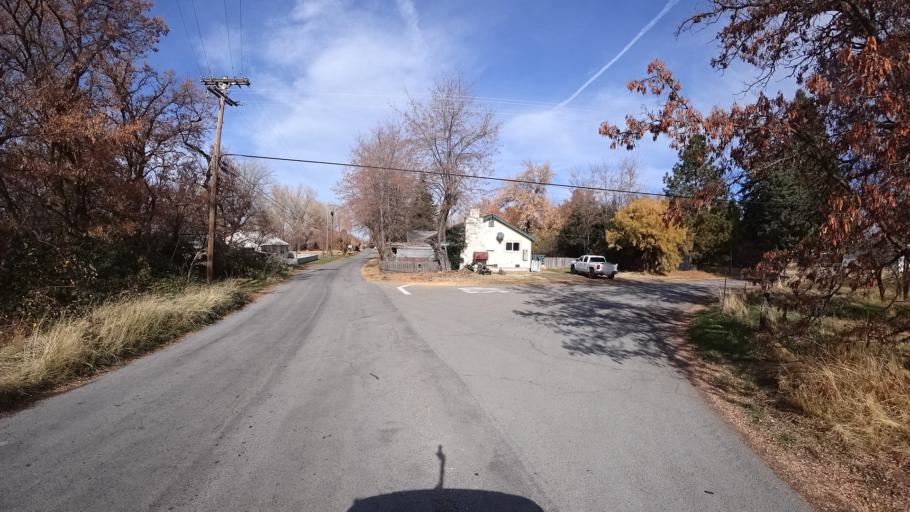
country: US
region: California
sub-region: Siskiyou County
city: Weed
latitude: 41.4584
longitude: -122.4324
